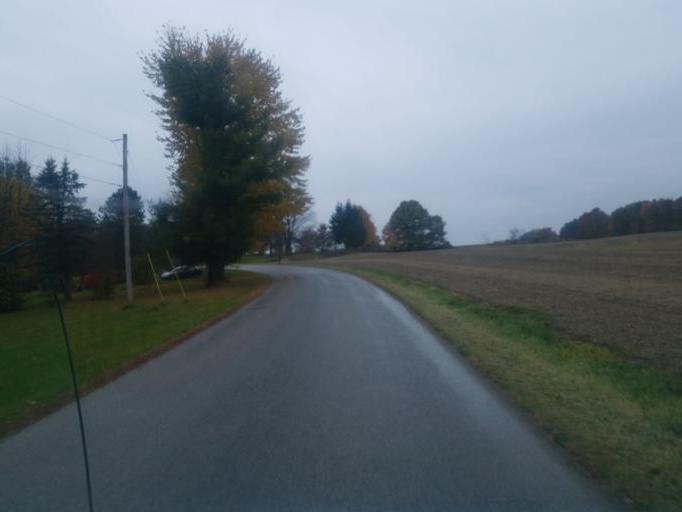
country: US
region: Ohio
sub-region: Morrow County
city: Mount Gilead
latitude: 40.5361
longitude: -82.8038
